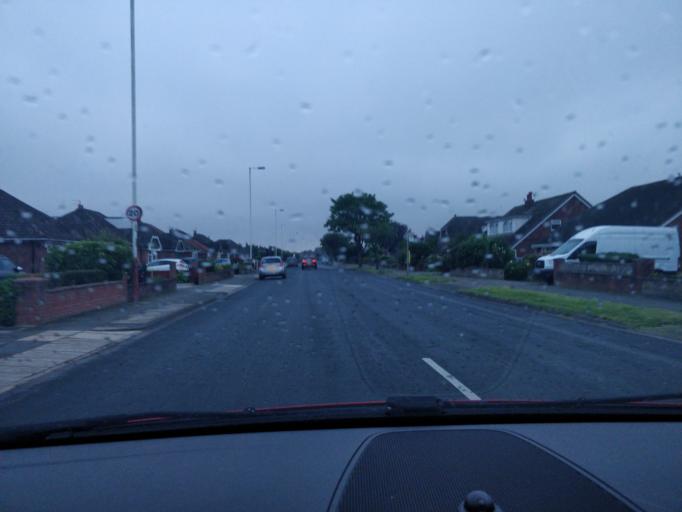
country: GB
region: England
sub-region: Lancashire
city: Banks
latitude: 53.6740
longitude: -2.9548
